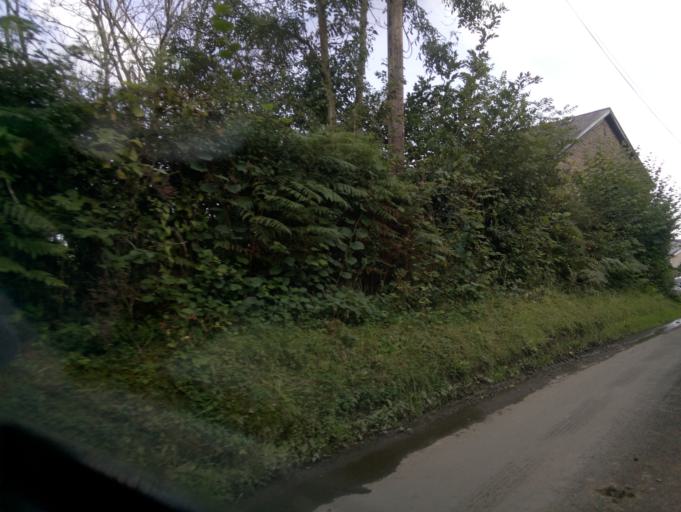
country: GB
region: Wales
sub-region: Cardiff
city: Pentyrch
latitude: 51.5505
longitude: -3.2776
